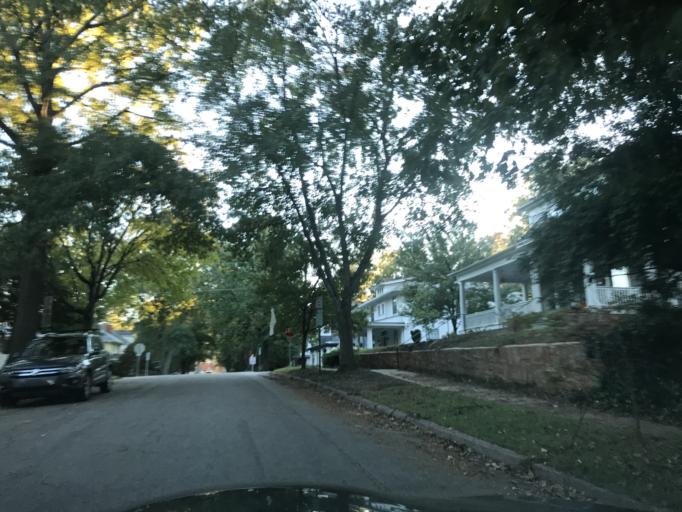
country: US
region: North Carolina
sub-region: Wake County
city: West Raleigh
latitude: 35.7861
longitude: -78.6574
